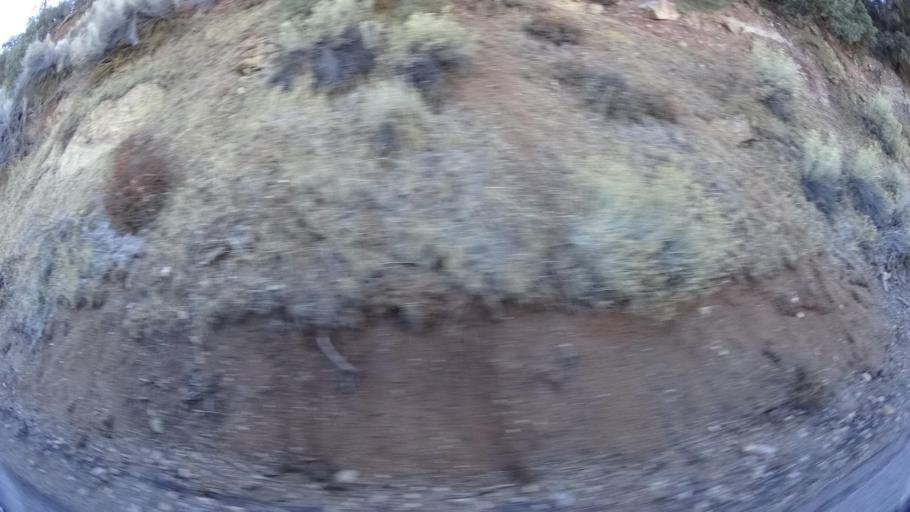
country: US
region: California
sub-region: Kern County
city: Maricopa
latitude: 34.8799
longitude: -119.3508
